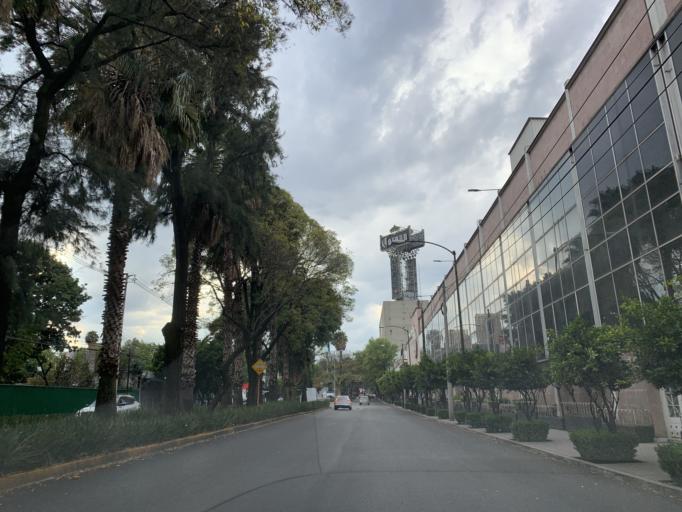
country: MX
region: Mexico City
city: Miguel Hidalgo
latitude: 19.4403
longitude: -99.1881
